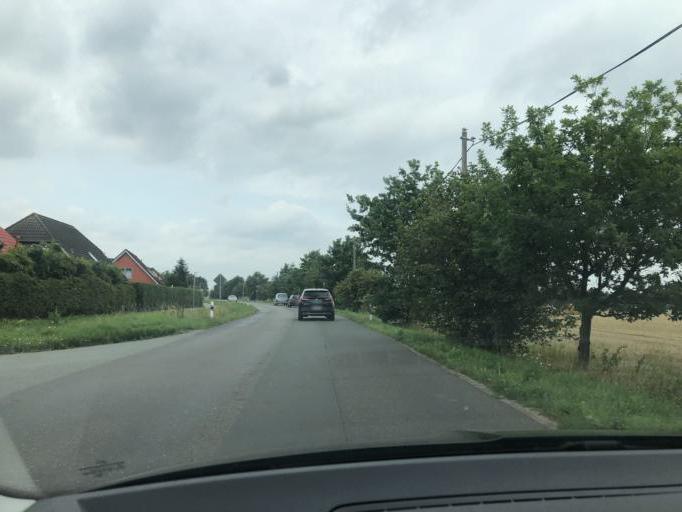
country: DE
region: Mecklenburg-Vorpommern
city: Klein Rogahn
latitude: 53.5701
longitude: 11.3514
